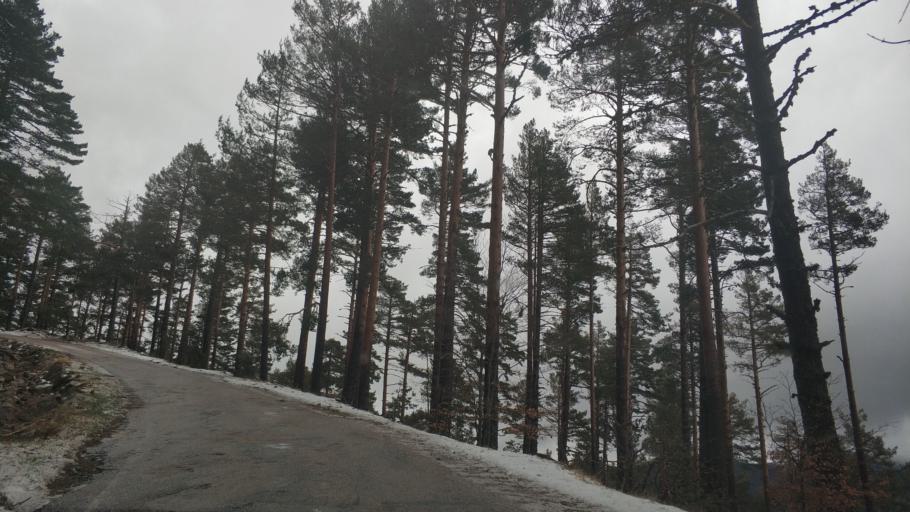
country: ES
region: Castille and Leon
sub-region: Provincia de Burgos
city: Neila
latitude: 42.0470
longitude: -3.0260
